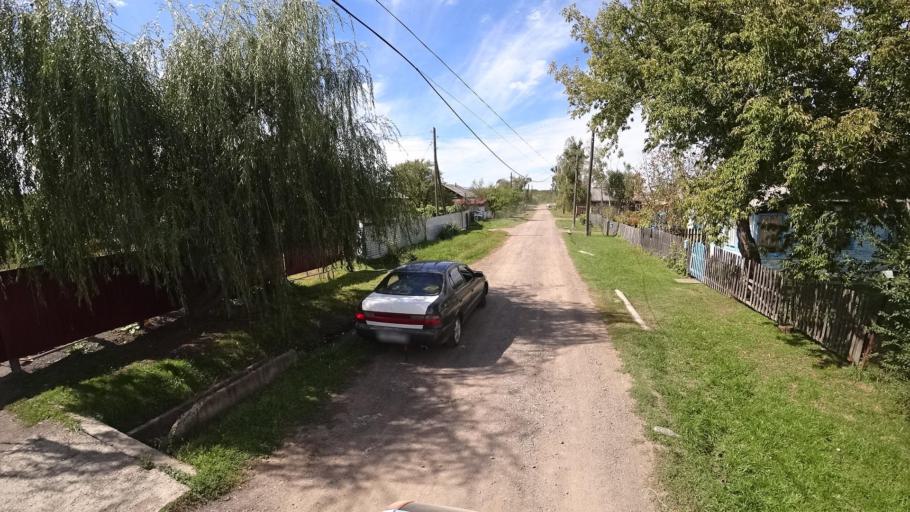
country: RU
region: Primorskiy
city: Yakovlevka
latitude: 44.4317
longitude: 133.5610
